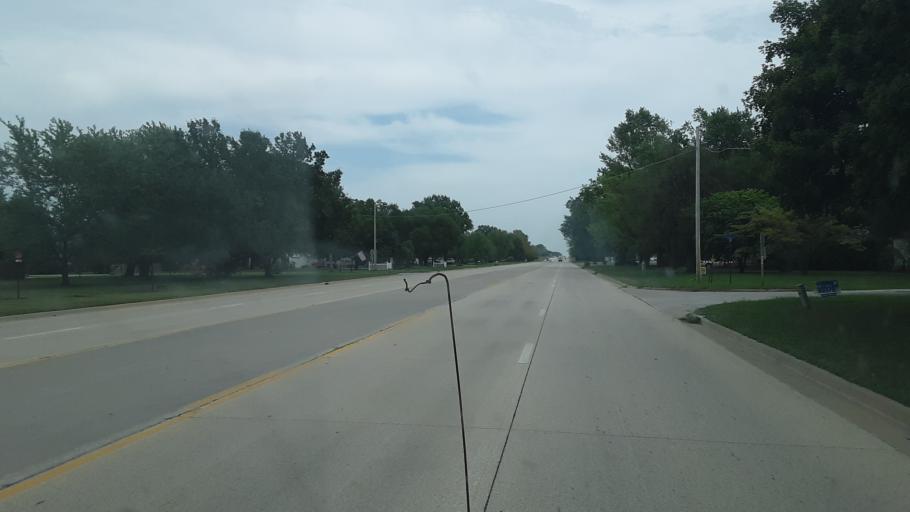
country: US
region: Kansas
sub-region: Allen County
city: Iola
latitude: 37.9220
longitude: -95.3680
